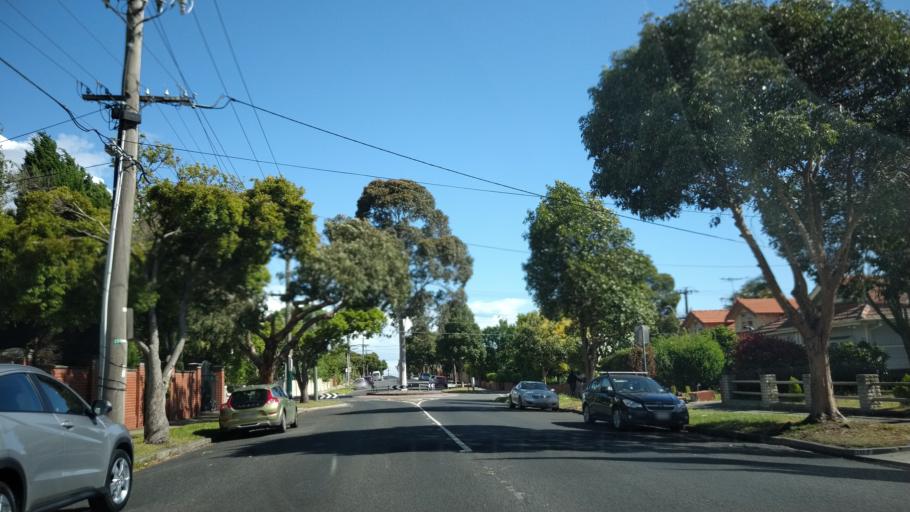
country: AU
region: Victoria
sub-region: Glen Eira
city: Caulfield
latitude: -37.8851
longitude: 145.0339
